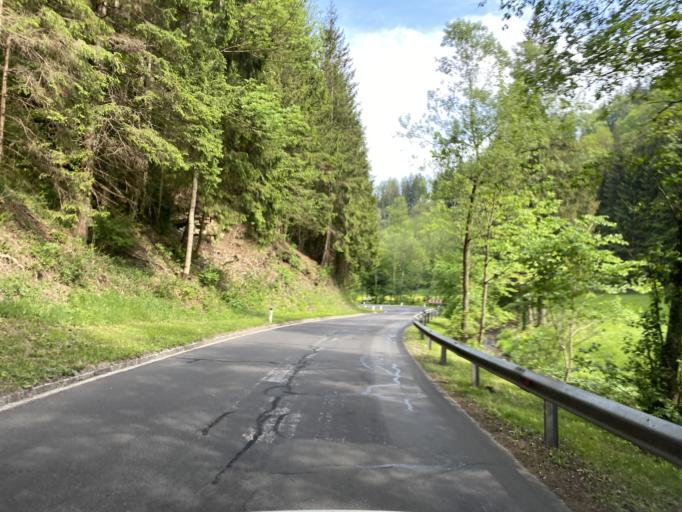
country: AT
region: Styria
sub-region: Politischer Bezirk Weiz
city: Koglhof
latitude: 47.3059
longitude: 15.6638
